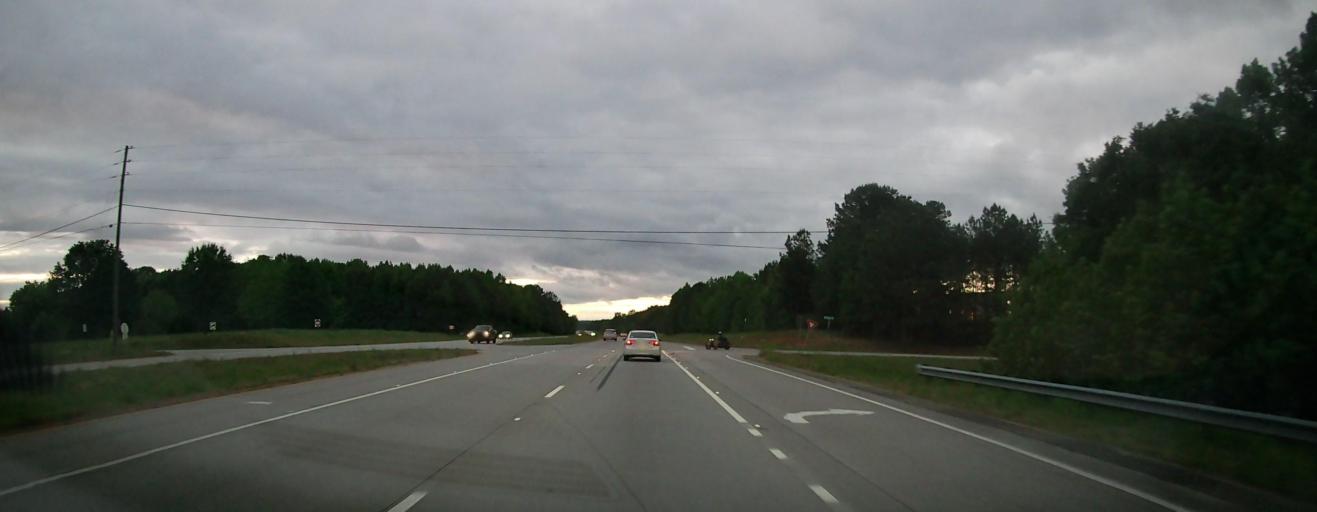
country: US
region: Georgia
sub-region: Jackson County
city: Arcade
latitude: 34.0797
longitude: -83.5751
